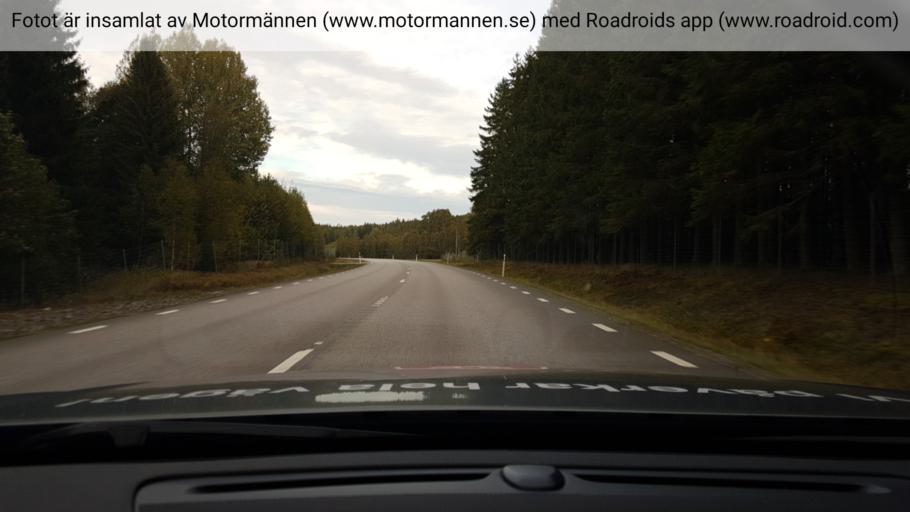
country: SE
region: Vaestra Goetaland
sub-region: Bengtsfors Kommun
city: Dals Langed
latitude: 59.0224
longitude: 12.3796
